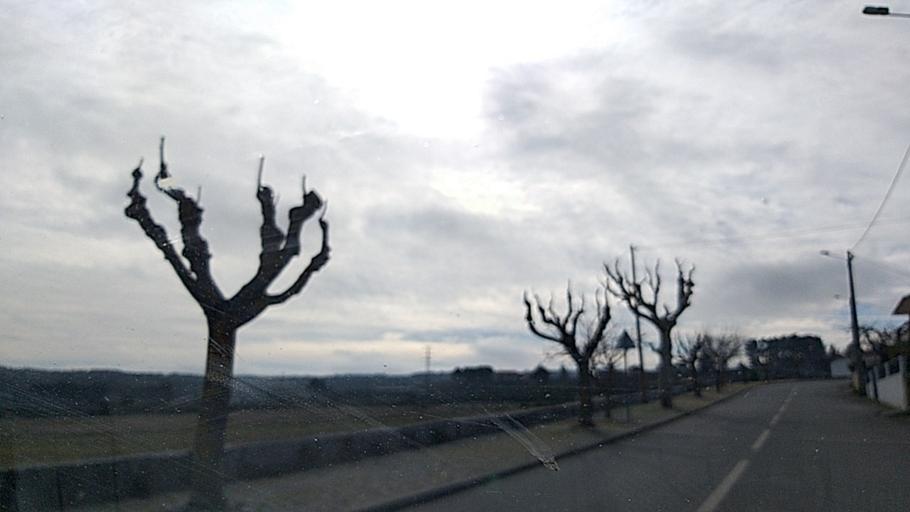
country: PT
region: Guarda
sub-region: Fornos de Algodres
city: Fornos de Algodres
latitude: 40.6798
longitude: -7.5305
